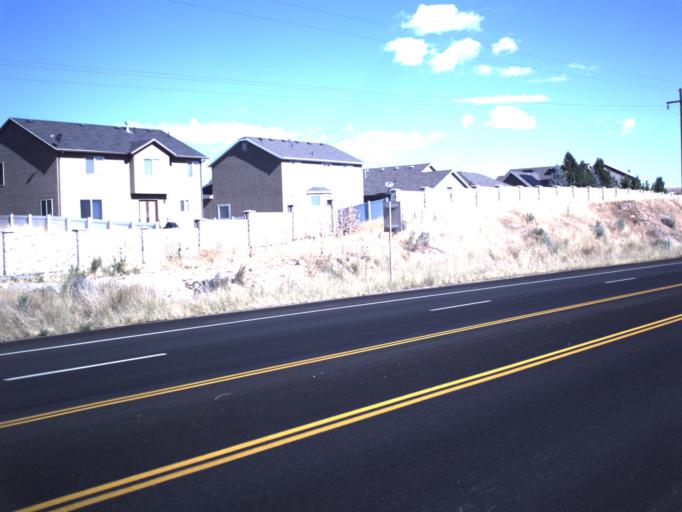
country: US
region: Utah
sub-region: Salt Lake County
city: Oquirrh
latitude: 40.6064
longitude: -112.0560
